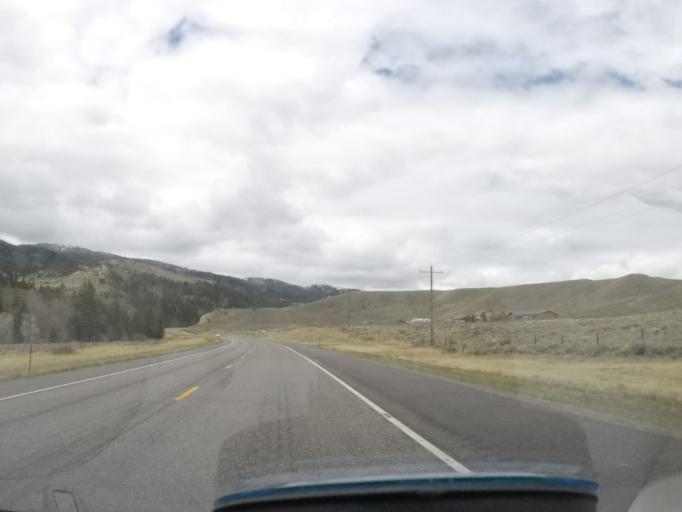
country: US
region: Wyoming
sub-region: Sublette County
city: Pinedale
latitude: 43.5793
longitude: -109.7469
